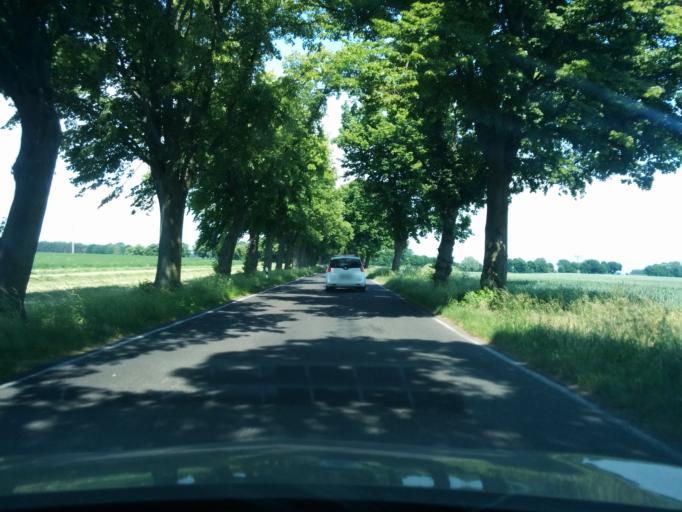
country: DE
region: Brandenburg
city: Bernau bei Berlin
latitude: 52.6400
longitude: 13.5745
